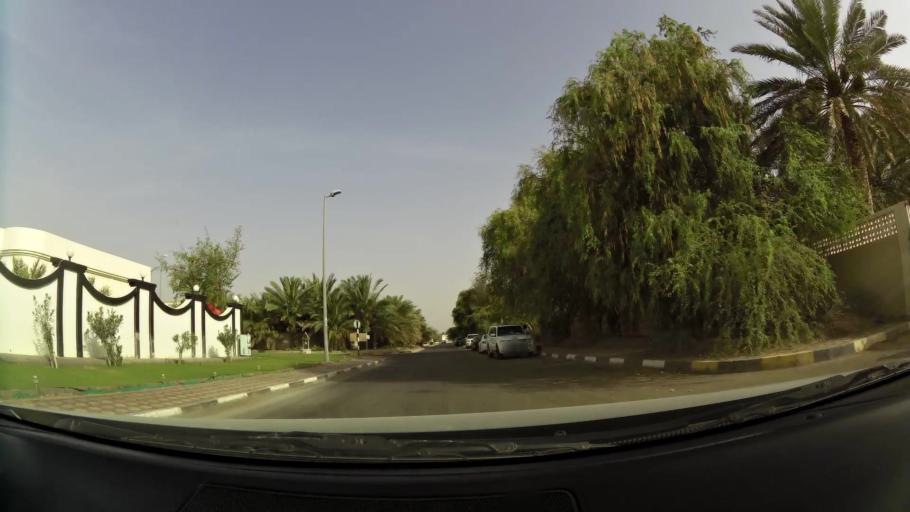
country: AE
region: Abu Dhabi
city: Al Ain
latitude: 24.1353
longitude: 55.6948
